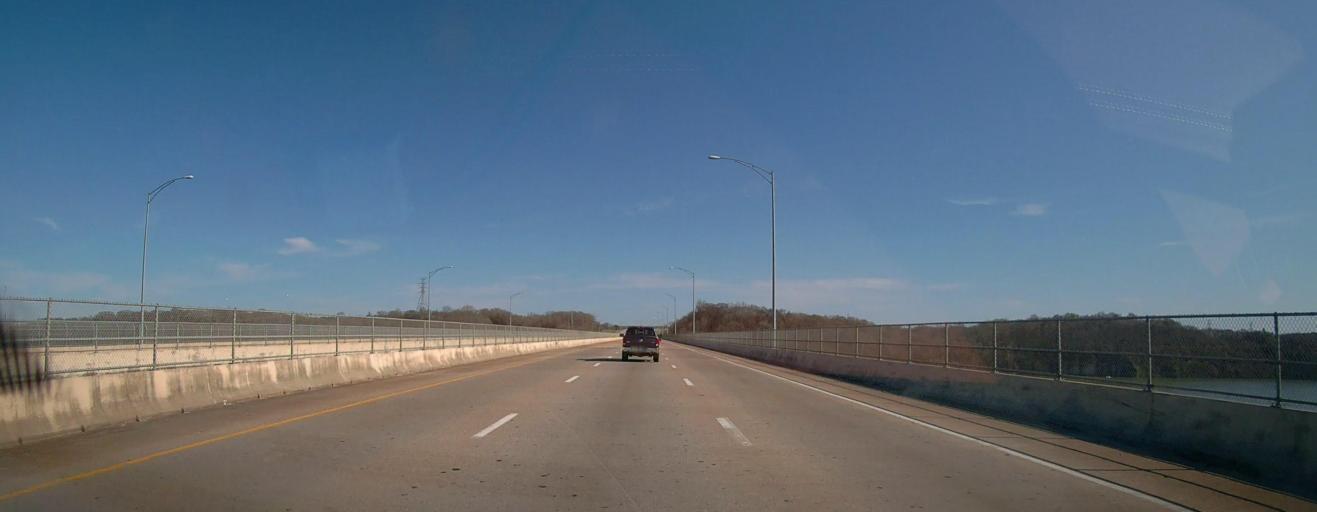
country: US
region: Alabama
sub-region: Lauderdale County
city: East Florence
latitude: 34.7957
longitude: -87.6462
